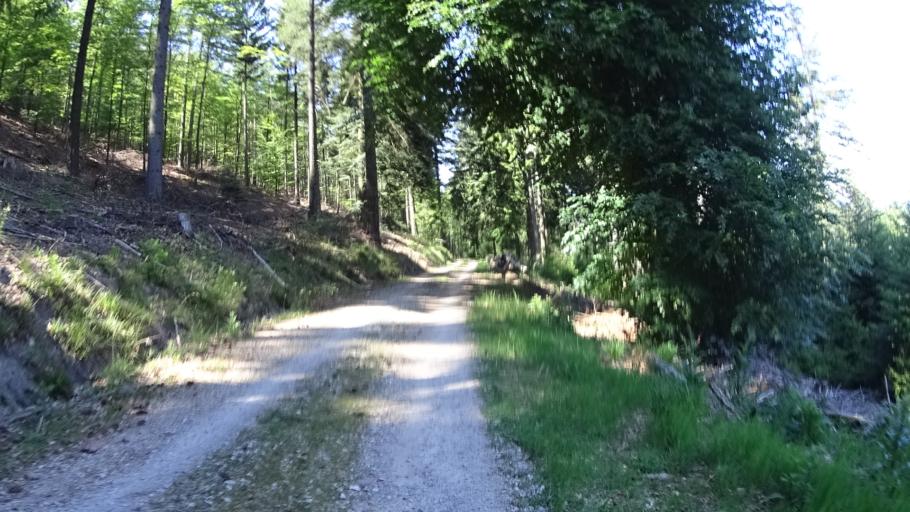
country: DE
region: Baden-Wuerttemberg
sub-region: Karlsruhe Region
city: Wilhelmsfeld
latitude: 49.4579
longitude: 8.7178
